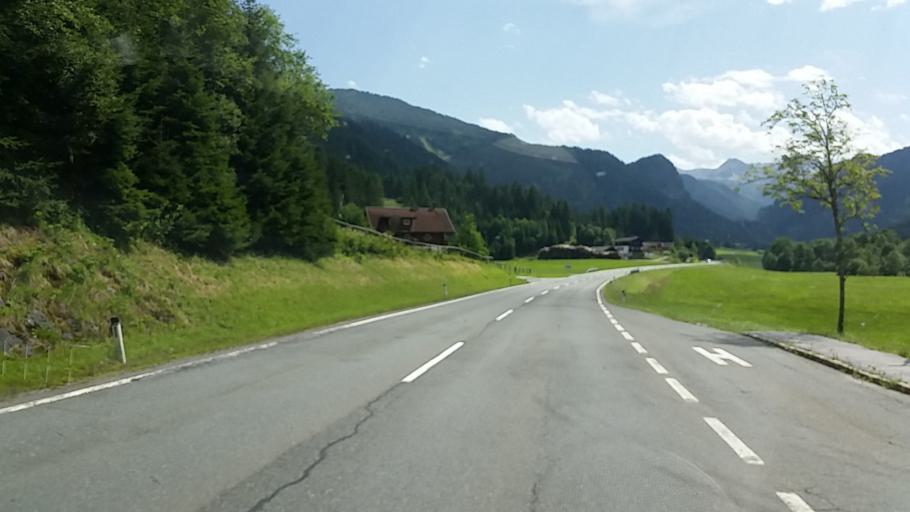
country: AT
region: Salzburg
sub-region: Politischer Bezirk Sankt Johann im Pongau
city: Untertauern
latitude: 47.3238
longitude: 13.5089
